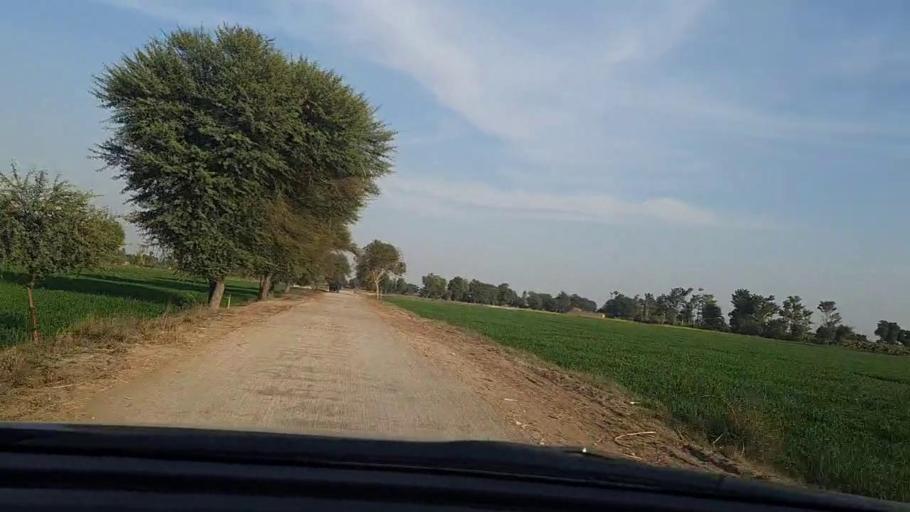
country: PK
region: Sindh
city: Daulatpur
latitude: 26.3369
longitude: 68.0344
